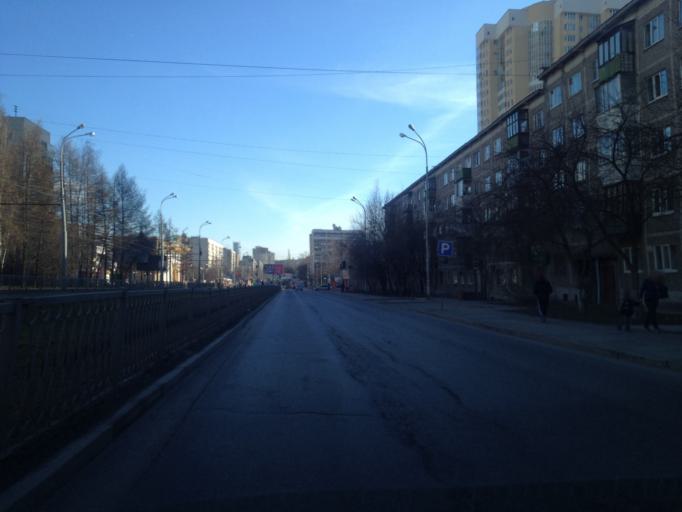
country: RU
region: Sverdlovsk
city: Sovkhoznyy
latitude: 56.8146
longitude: 60.5611
